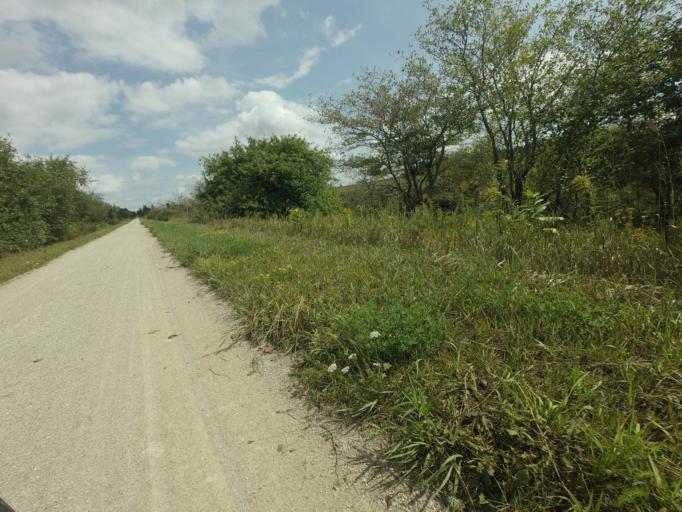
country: CA
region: Ontario
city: North Perth
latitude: 43.5762
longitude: -80.8095
